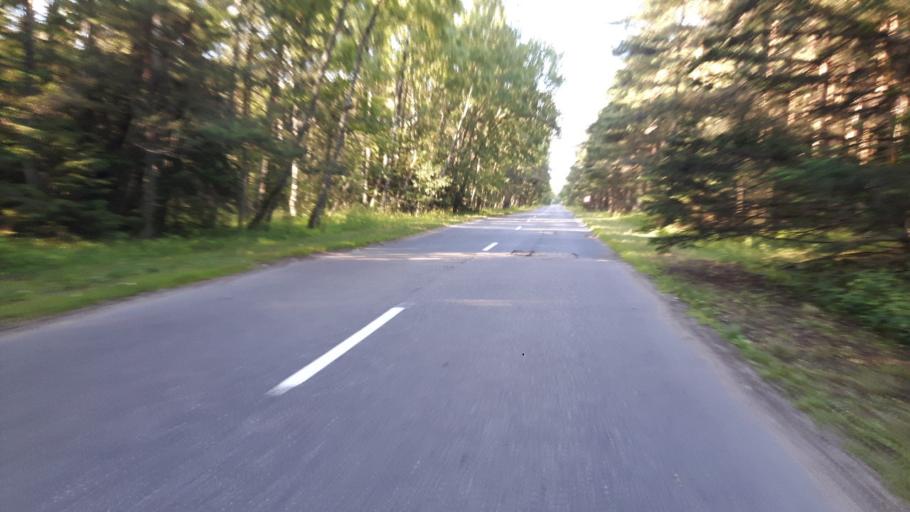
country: LT
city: Nida
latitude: 55.2324
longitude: 20.9041
